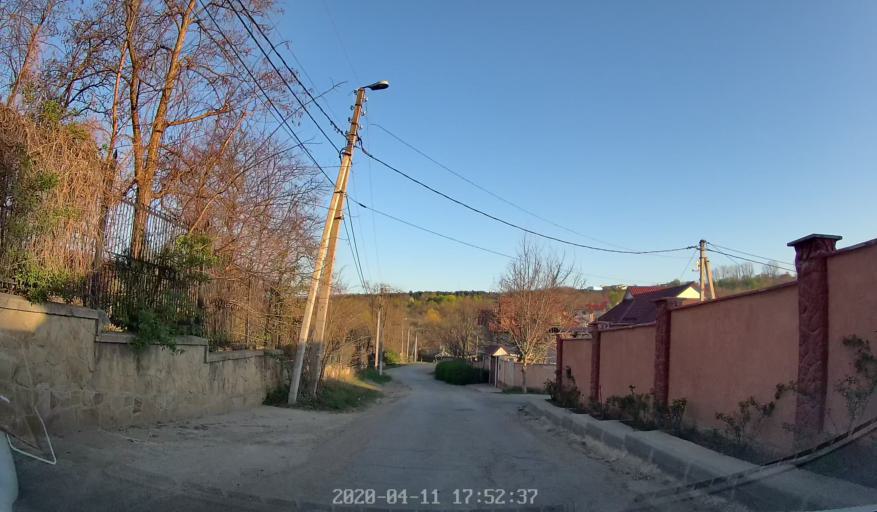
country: MD
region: Chisinau
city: Chisinau
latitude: 46.9724
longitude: 28.8643
